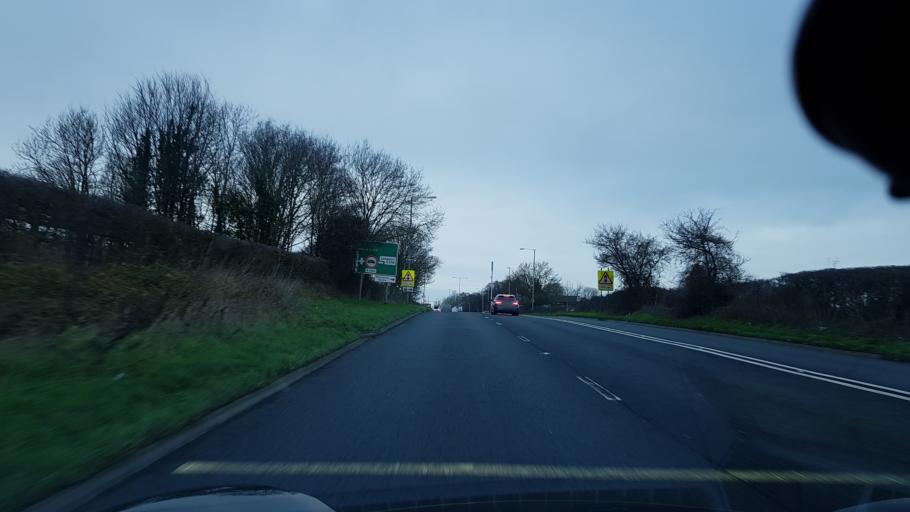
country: GB
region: England
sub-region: Somerset
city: Creech Saint Michael
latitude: 50.9975
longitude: -3.0184
